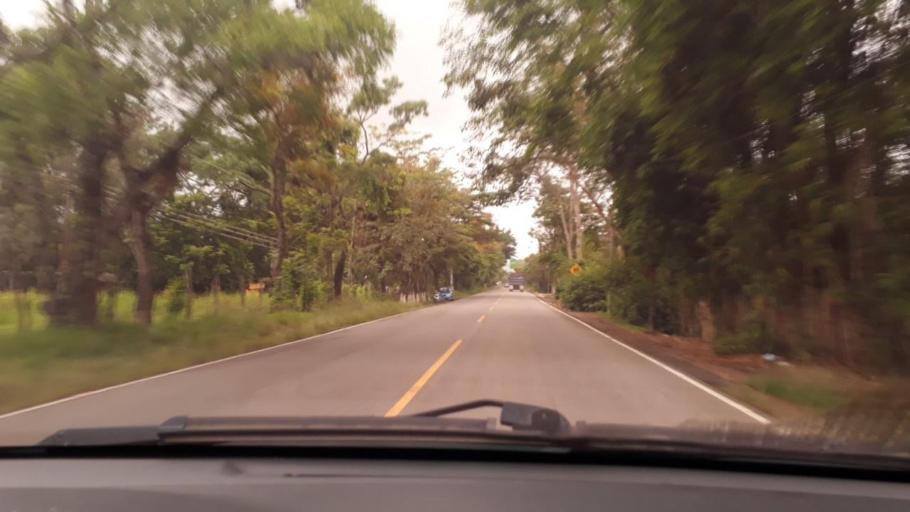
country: GT
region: Chiquimula
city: Esquipulas
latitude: 14.5653
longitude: -89.3181
